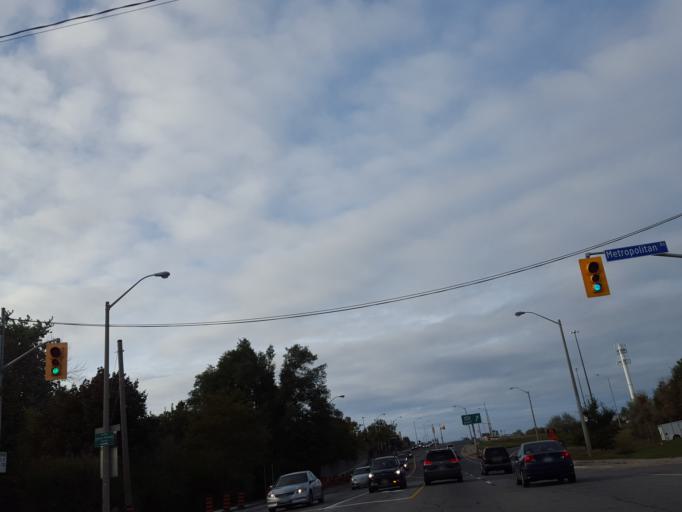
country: CA
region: Ontario
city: Scarborough
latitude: 43.7671
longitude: -79.3027
